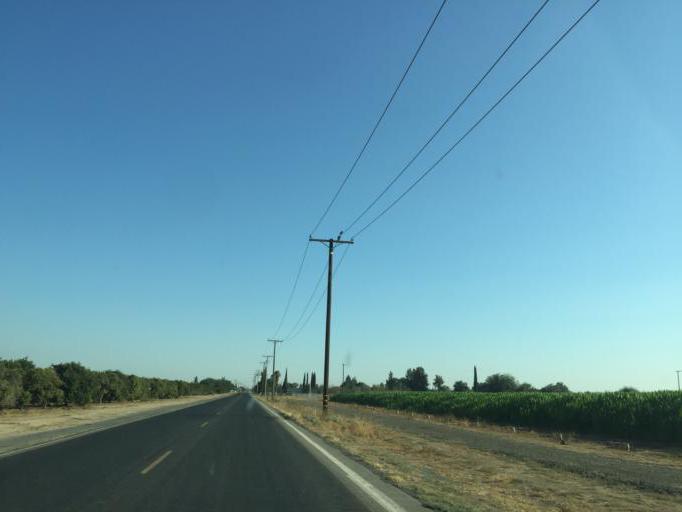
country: US
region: California
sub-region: Tulare County
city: Ivanhoe
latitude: 36.4050
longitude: -119.2783
